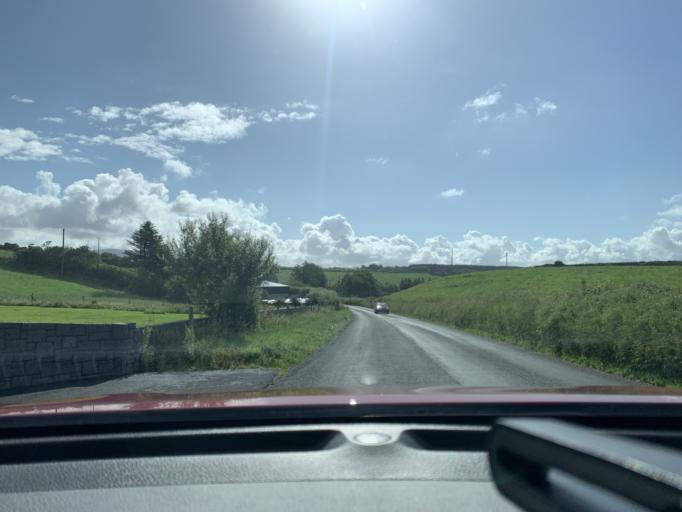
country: IE
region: Connaught
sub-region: Sligo
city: Strandhill
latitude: 54.3539
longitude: -8.6042
